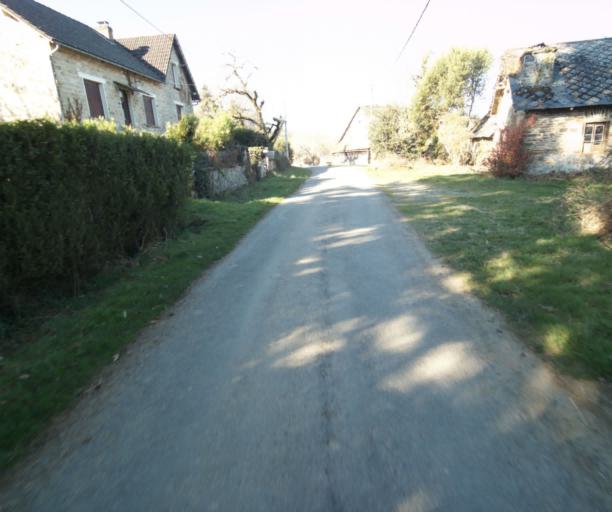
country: FR
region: Limousin
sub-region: Departement de la Correze
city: Saint-Clement
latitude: 45.3723
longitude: 1.6542
